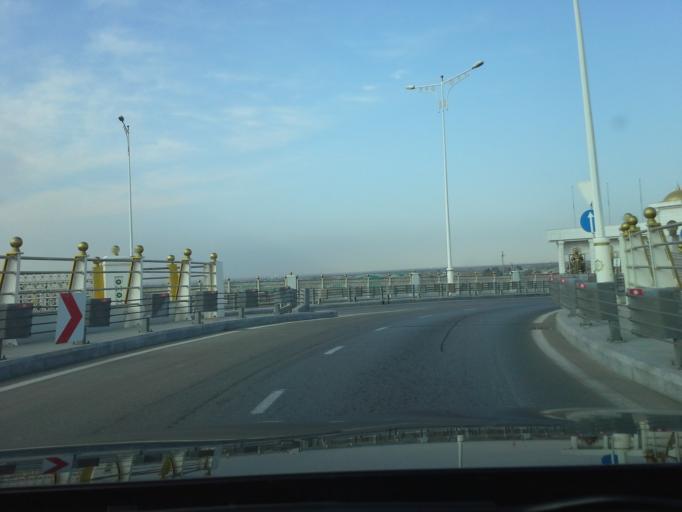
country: TM
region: Ahal
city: Abadan
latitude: 38.0882
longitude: 58.1124
